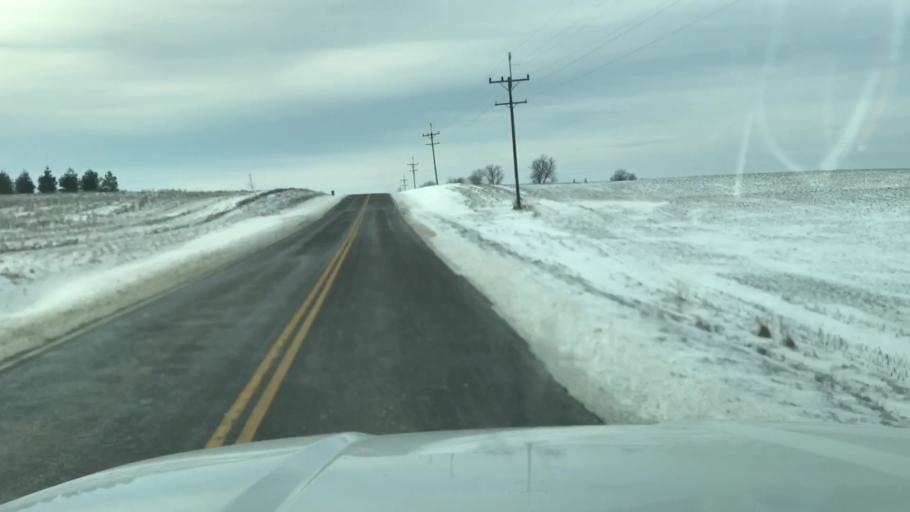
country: US
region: Missouri
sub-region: Holt County
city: Mound City
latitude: 40.1051
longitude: -95.1448
